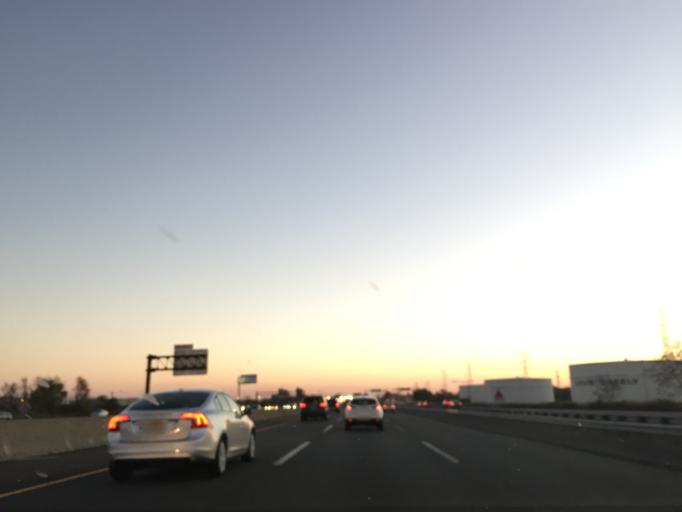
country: US
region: New Jersey
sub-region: Union County
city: Linden
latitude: 40.6068
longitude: -74.2271
